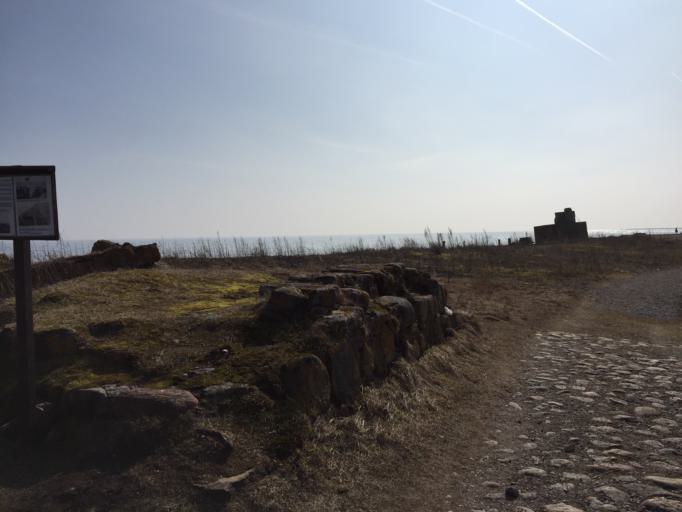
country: LV
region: Dundaga
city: Dundaga
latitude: 57.9088
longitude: 22.0550
